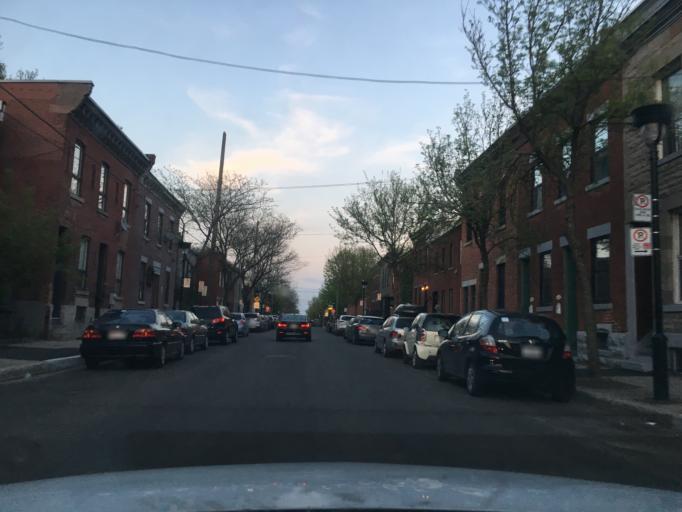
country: CA
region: Quebec
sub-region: Montreal
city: Montreal
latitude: 45.4806
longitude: -73.5576
